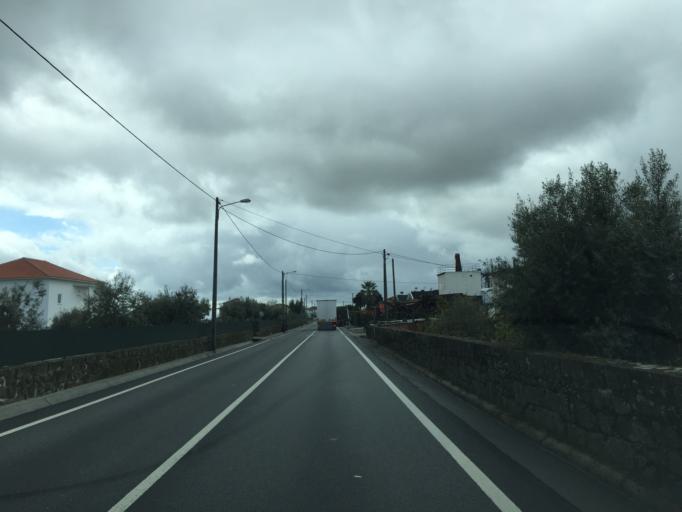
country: PT
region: Coimbra
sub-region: Oliveira do Hospital
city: Oliveira do Hospital
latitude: 40.3153
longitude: -7.9001
